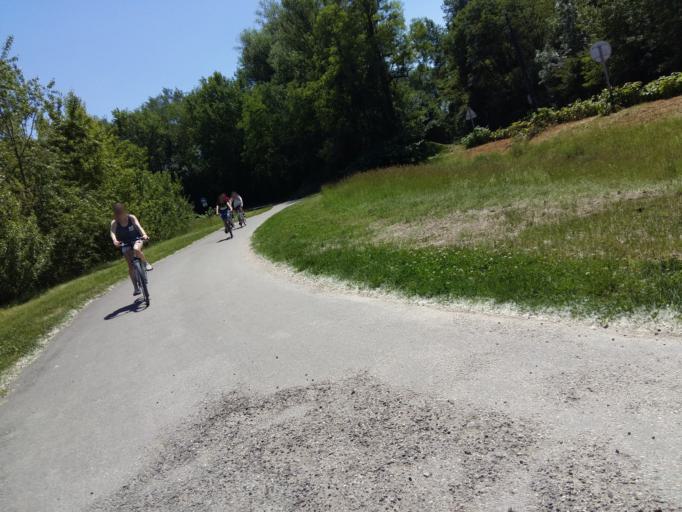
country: FR
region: Rhone-Alpes
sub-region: Departement du Rhone
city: Decines-Charpieu
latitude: 45.7977
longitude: 4.9702
